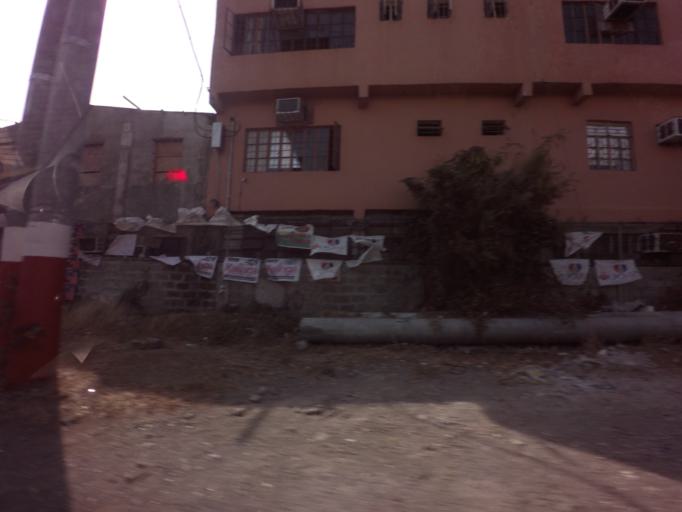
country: PH
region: Calabarzon
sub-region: Province of Rizal
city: Taguig
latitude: 14.5145
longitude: 121.0480
